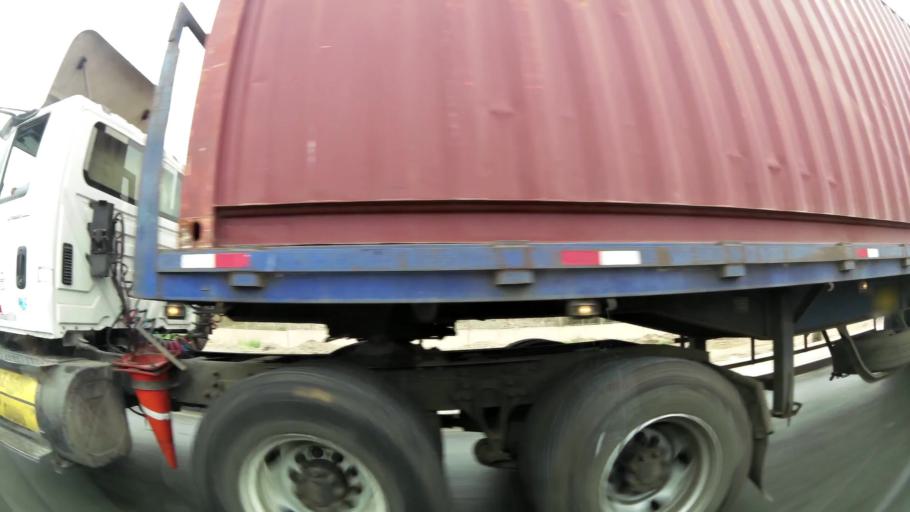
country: PE
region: Callao
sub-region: Callao
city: Callao
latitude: -12.0321
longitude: -77.1273
